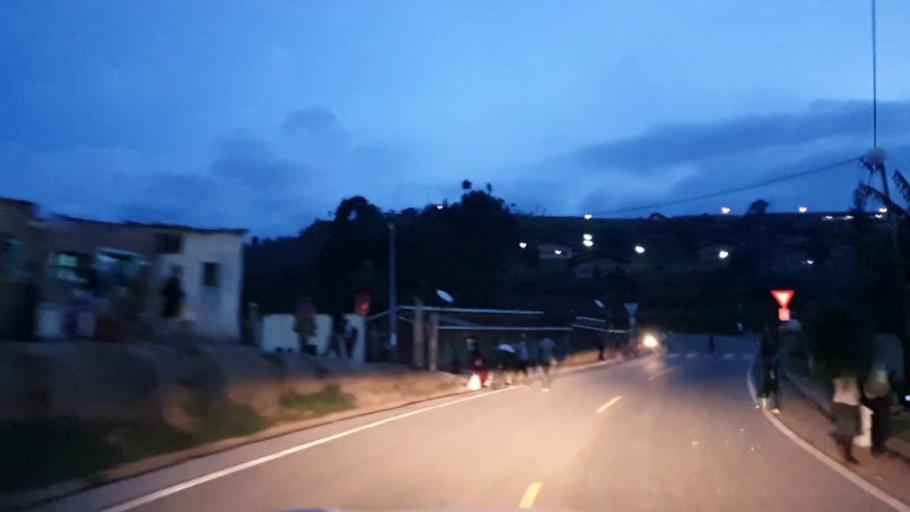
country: RW
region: Southern Province
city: Gikongoro
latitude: -2.4649
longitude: 29.5673
